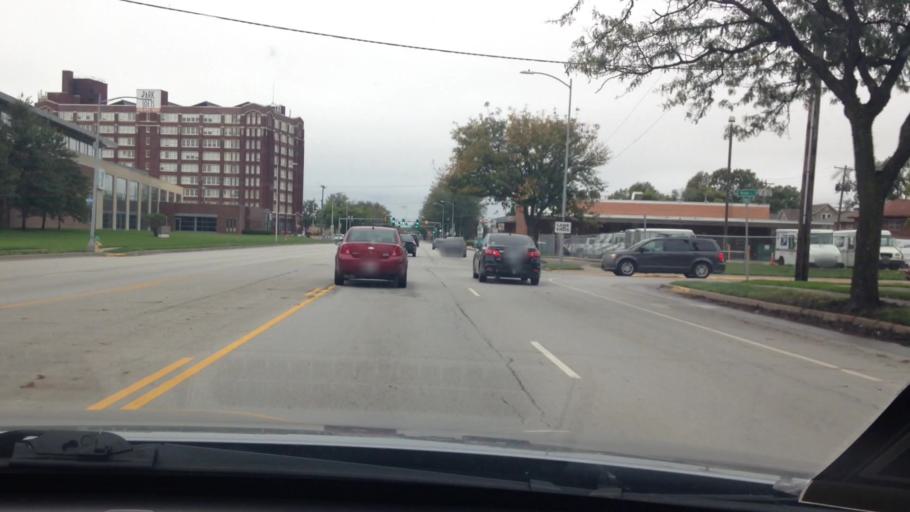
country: US
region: Missouri
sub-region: Clay County
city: North Kansas City
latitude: 39.1435
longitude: -94.5687
